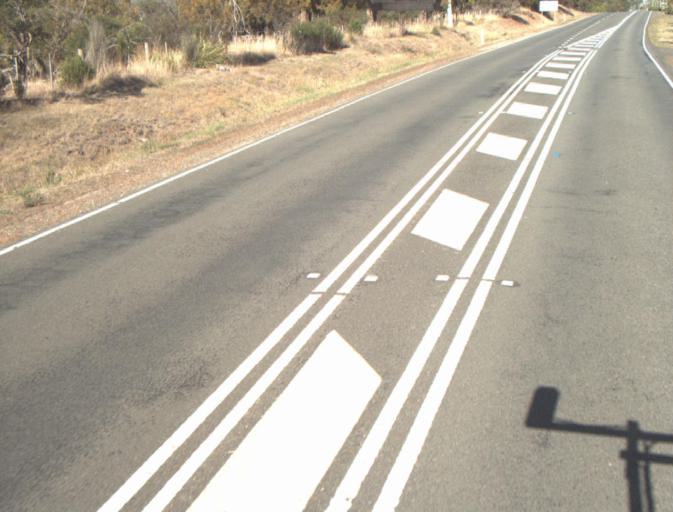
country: AU
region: Tasmania
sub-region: Launceston
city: Mayfield
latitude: -41.3315
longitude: 147.0739
